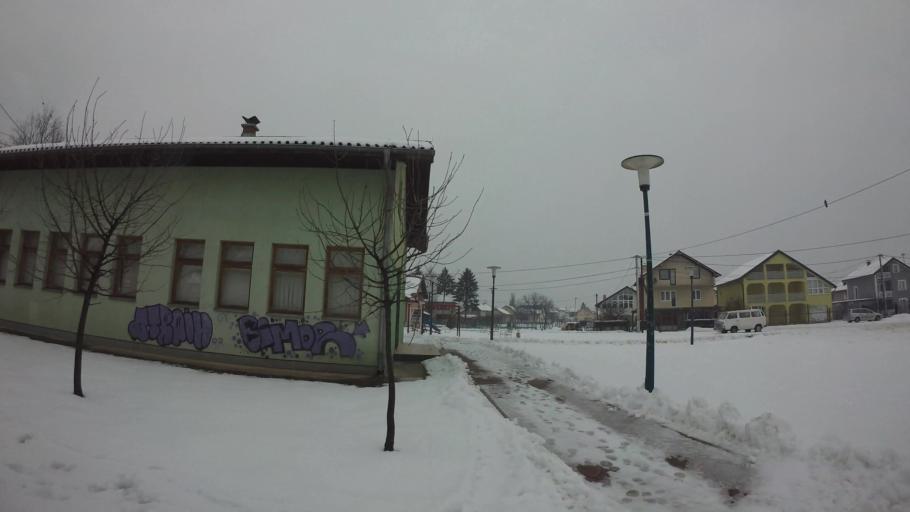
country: BA
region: Federation of Bosnia and Herzegovina
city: Hadzici
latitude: 43.8434
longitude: 18.2776
